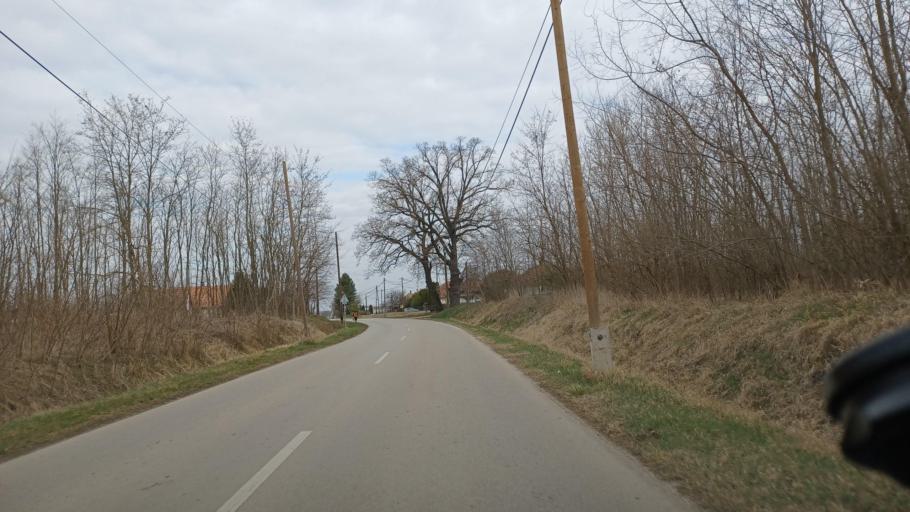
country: HU
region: Tolna
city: Tengelic
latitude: 46.5433
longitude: 18.7019
